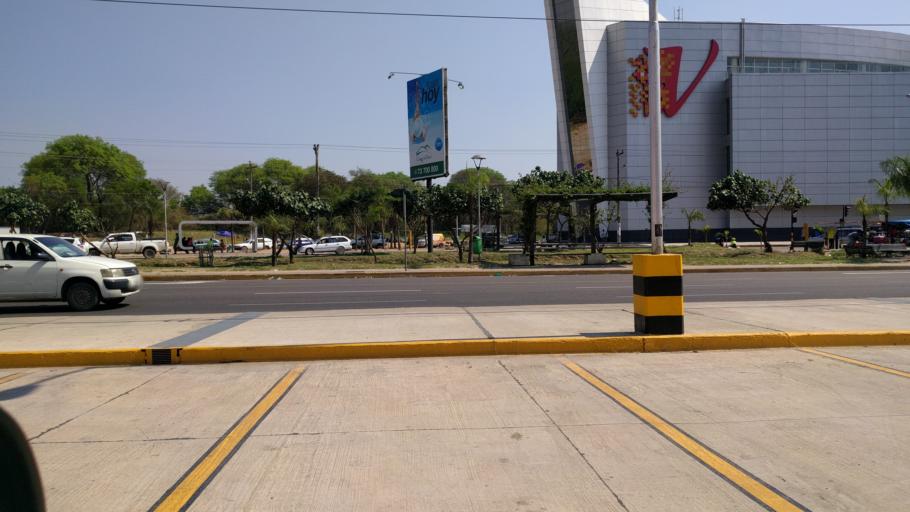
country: BO
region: Santa Cruz
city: Santa Cruz de la Sierra
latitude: -17.7563
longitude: -63.2003
